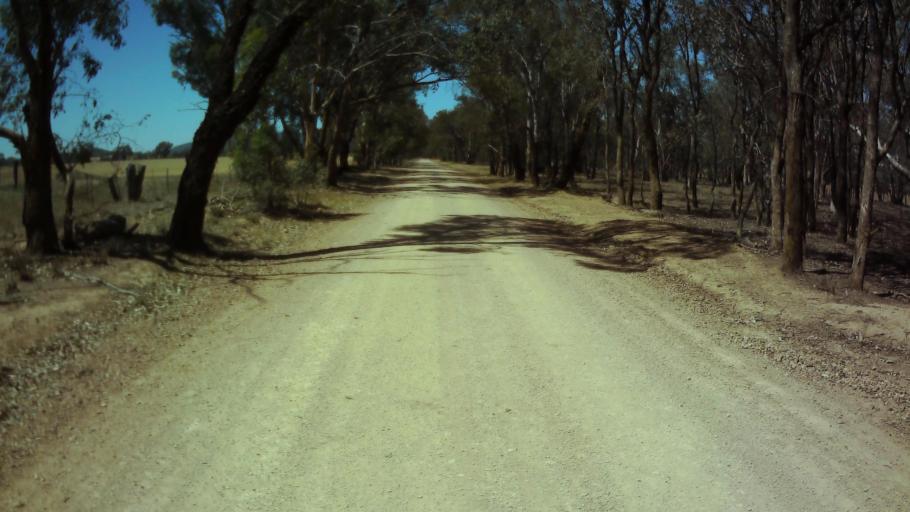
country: AU
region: New South Wales
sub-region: Weddin
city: Grenfell
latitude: -33.9150
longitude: 148.0794
